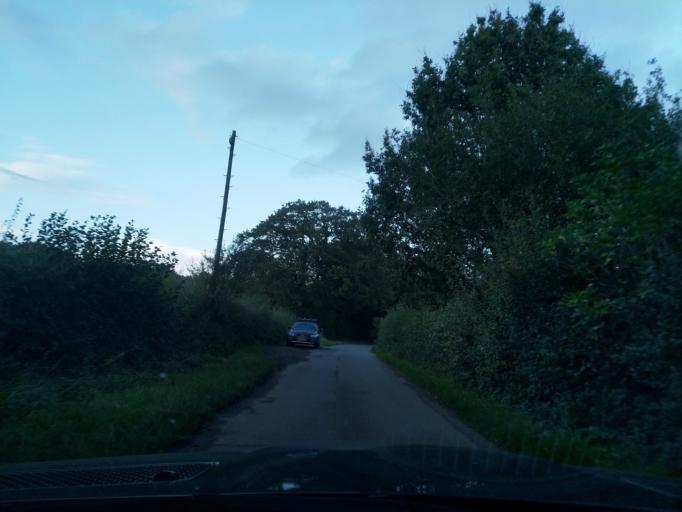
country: GB
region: England
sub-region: Warwickshire
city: Wroxall
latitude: 52.3447
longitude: -1.6649
